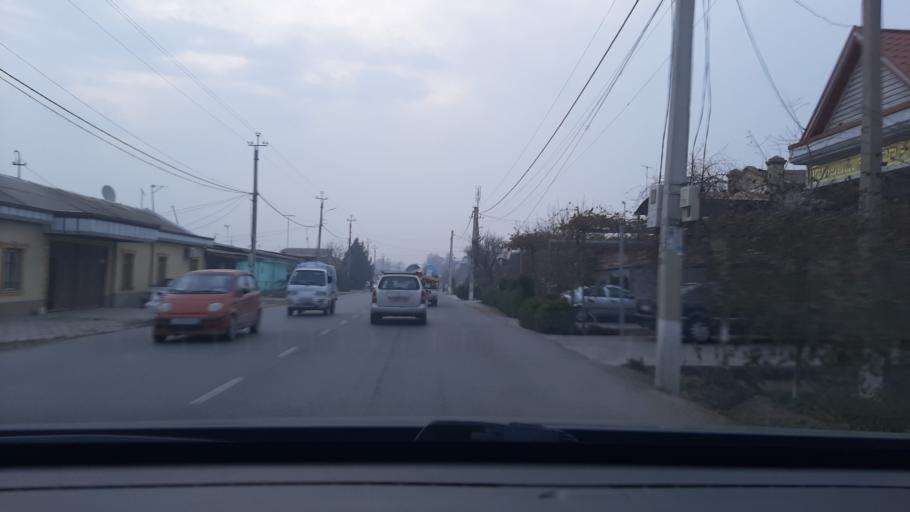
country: TJ
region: Viloyati Sughd
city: Khujand
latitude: 40.2626
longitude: 69.6015
